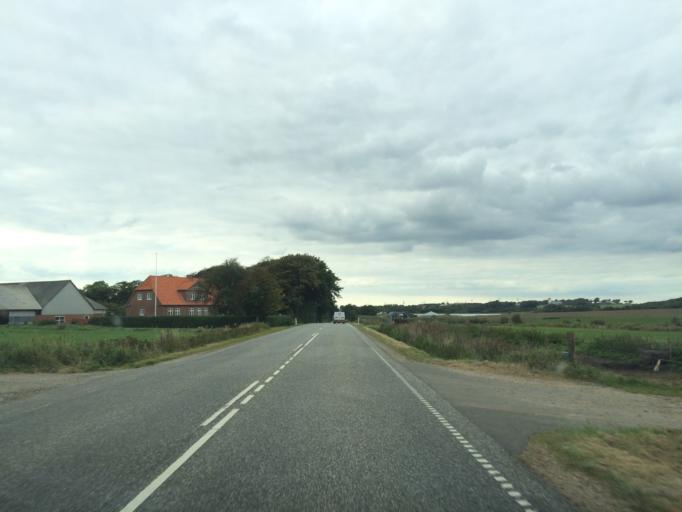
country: DK
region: Central Jutland
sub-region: Ringkobing-Skjern Kommune
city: Skjern
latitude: 56.0358
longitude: 8.4103
